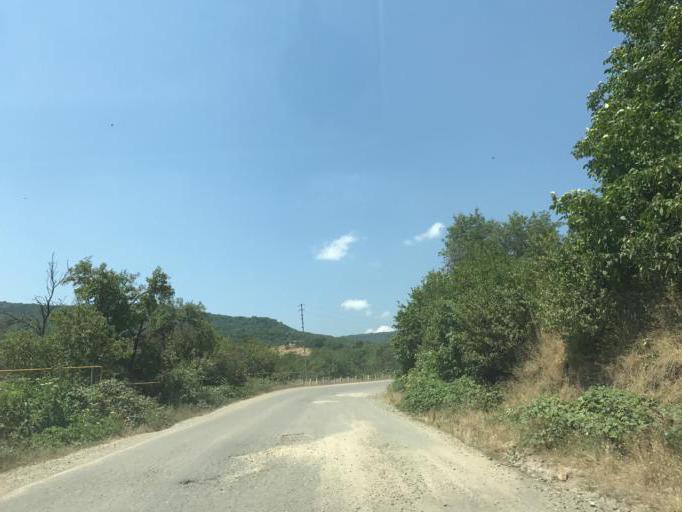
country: AZ
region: Tartar Rayon
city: Martakert
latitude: 40.1038
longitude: 46.6474
